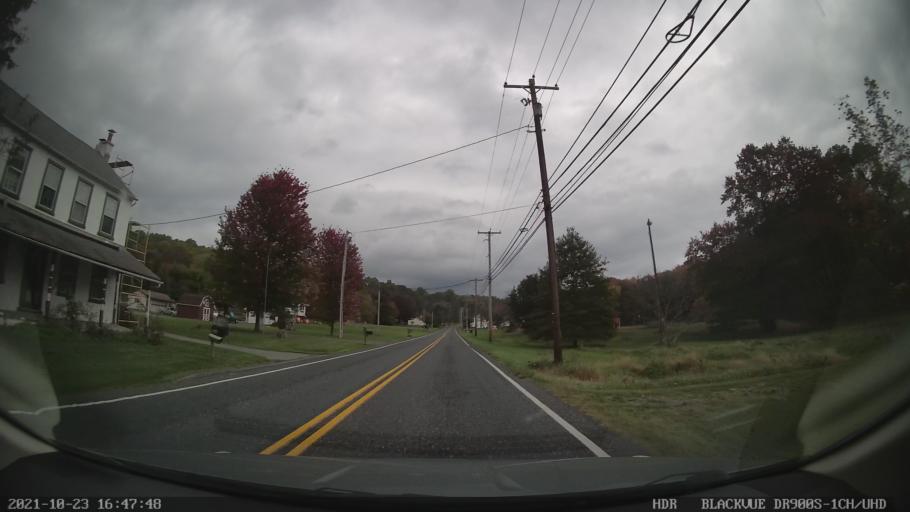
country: US
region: Pennsylvania
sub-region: Berks County
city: Red Lion
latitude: 40.4904
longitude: -75.6324
